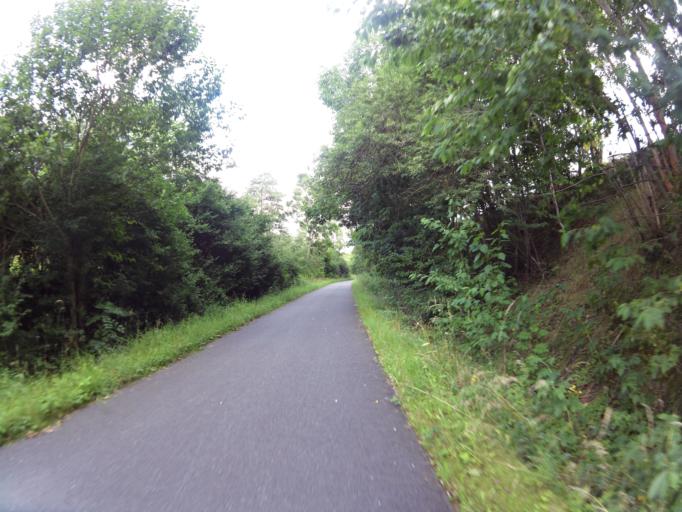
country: DE
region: Thuringia
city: Gorkwitz
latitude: 50.5758
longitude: 11.7909
